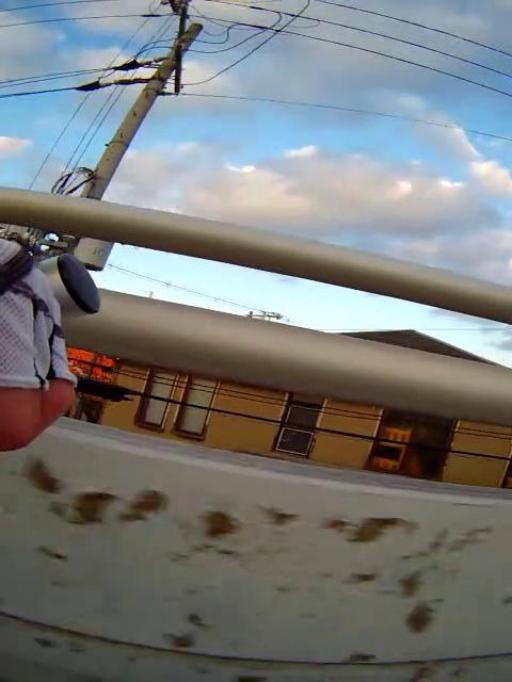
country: JP
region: Osaka
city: Osaka-shi
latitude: 34.7238
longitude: 135.4720
